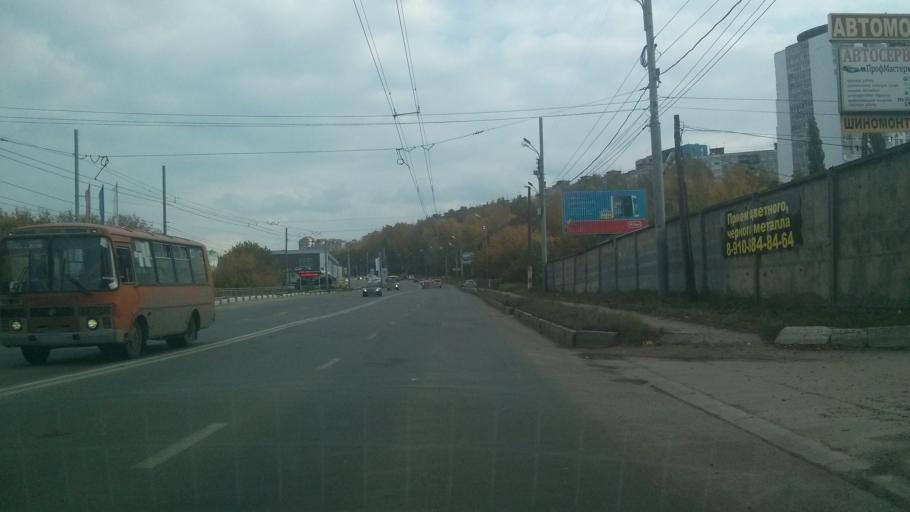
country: RU
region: Nizjnij Novgorod
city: Afonino
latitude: 56.3014
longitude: 44.0540
